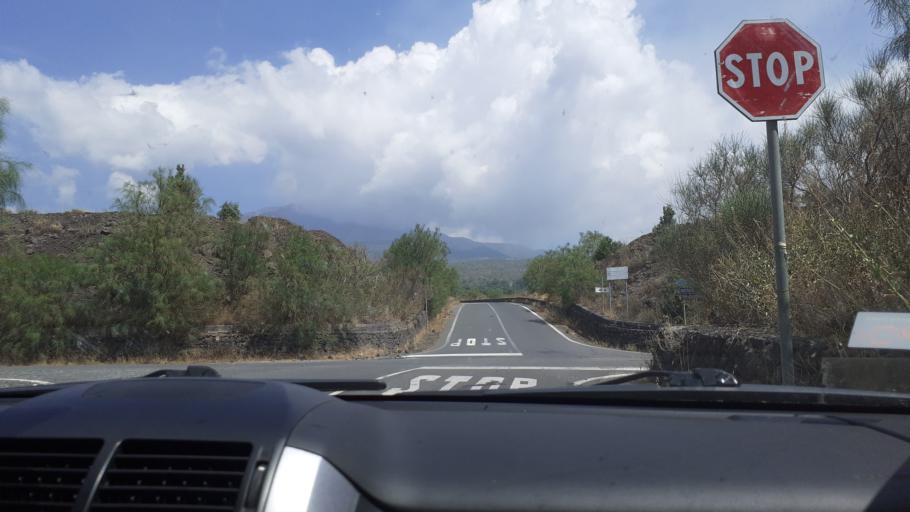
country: IT
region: Sicily
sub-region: Catania
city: Nicolosi
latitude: 37.6474
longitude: 15.0215
